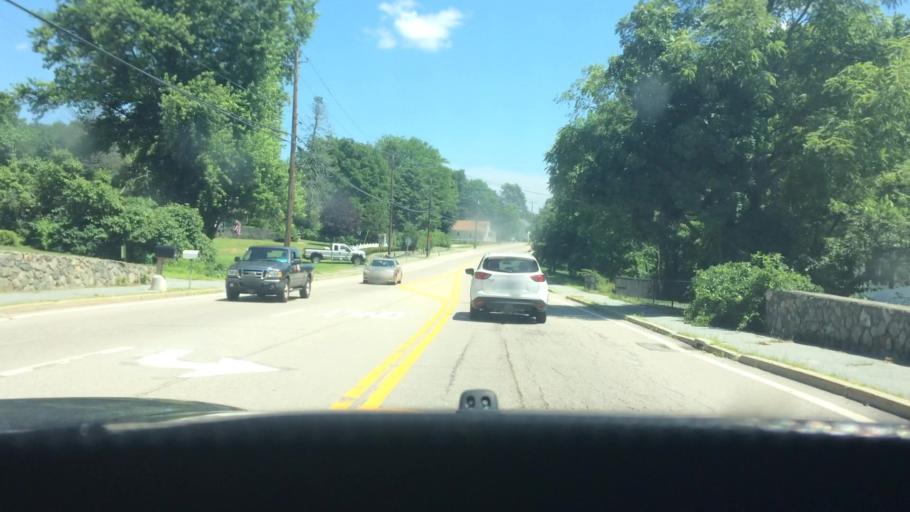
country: US
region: Massachusetts
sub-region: Worcester County
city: Millville
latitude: 42.0044
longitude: -71.5678
